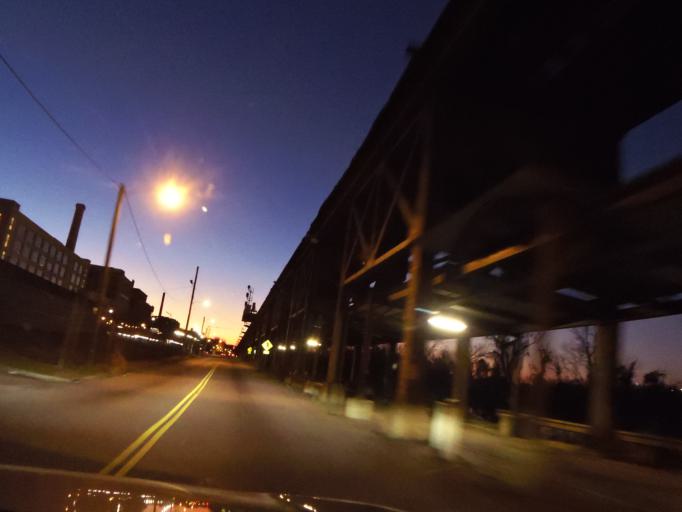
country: US
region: Virginia
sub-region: City of Richmond
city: Richmond
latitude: 37.5303
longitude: -77.4271
